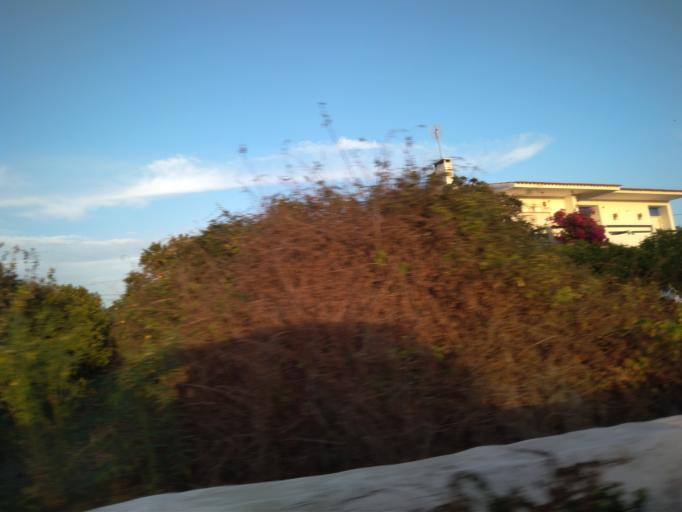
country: PT
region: Faro
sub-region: Faro
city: Santa Barbara de Nexe
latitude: 37.0699
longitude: -7.9580
